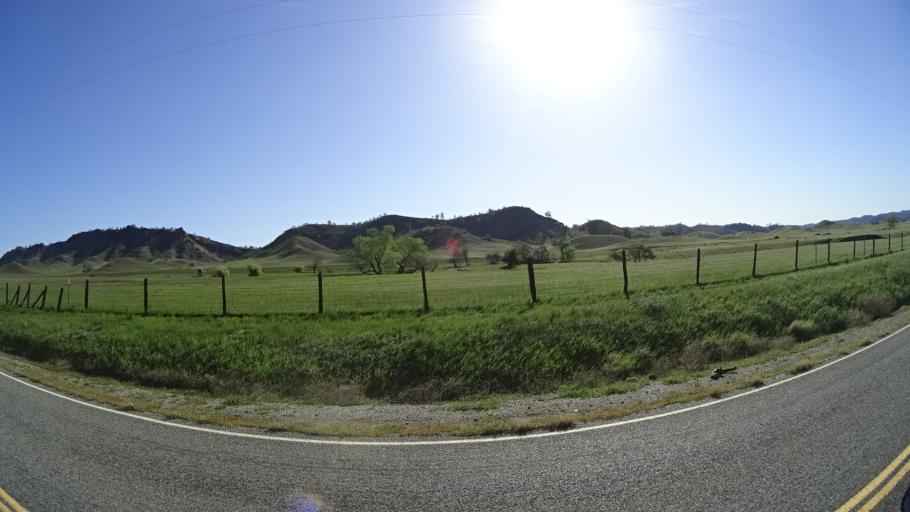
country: US
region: California
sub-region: Tehama County
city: Rancho Tehama Reserve
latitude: 39.7120
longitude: -122.5509
